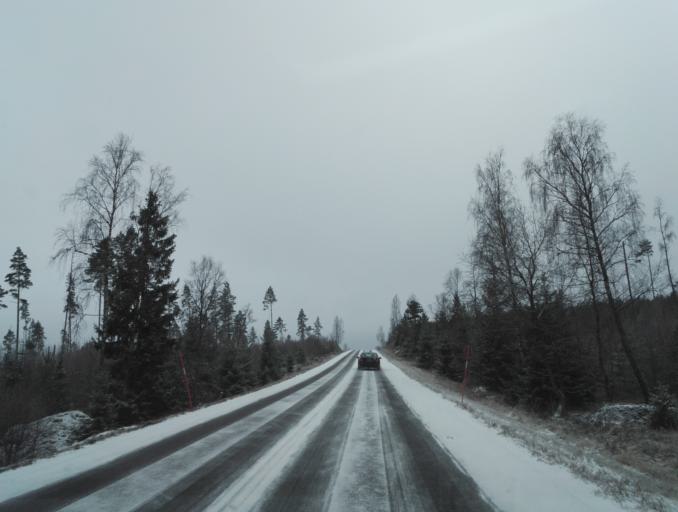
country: SE
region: Kronoberg
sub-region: Lessebo Kommun
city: Lessebo
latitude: 56.7768
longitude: 15.3009
